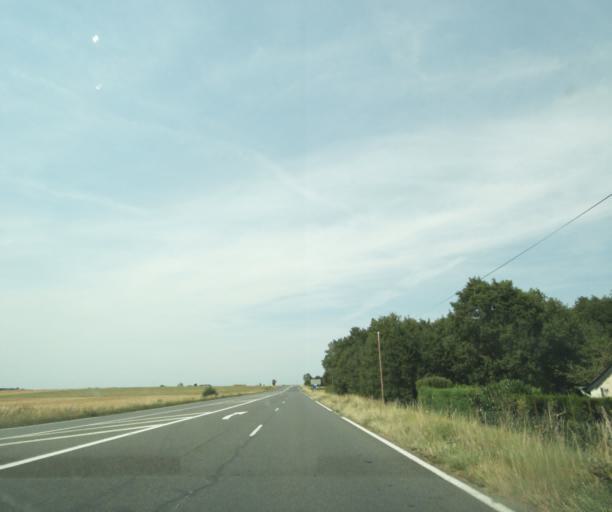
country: FR
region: Centre
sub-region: Departement d'Indre-et-Loire
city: Sainte-Maure-de-Touraine
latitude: 47.1531
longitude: 0.6464
